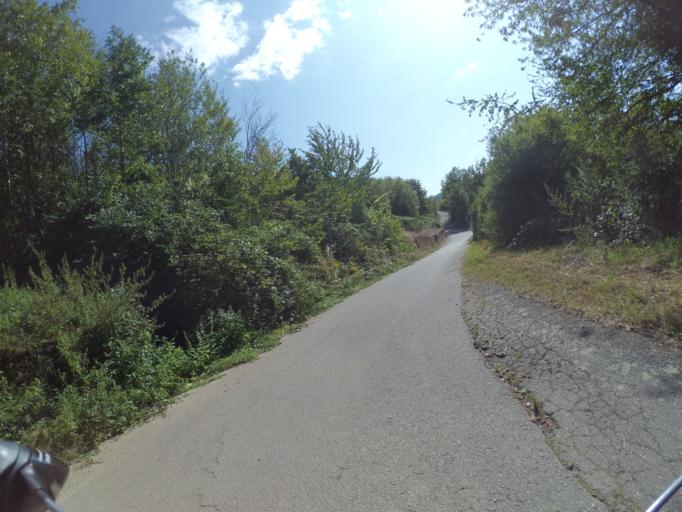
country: DE
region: Rheinland-Pfalz
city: Longuich
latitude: 49.8063
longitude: 6.7925
